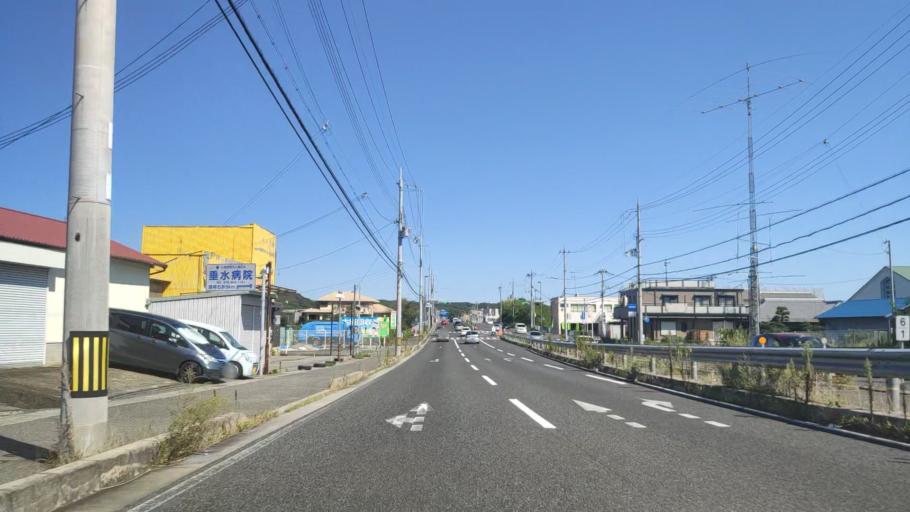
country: JP
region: Hyogo
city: Akashi
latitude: 34.7077
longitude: 134.9829
